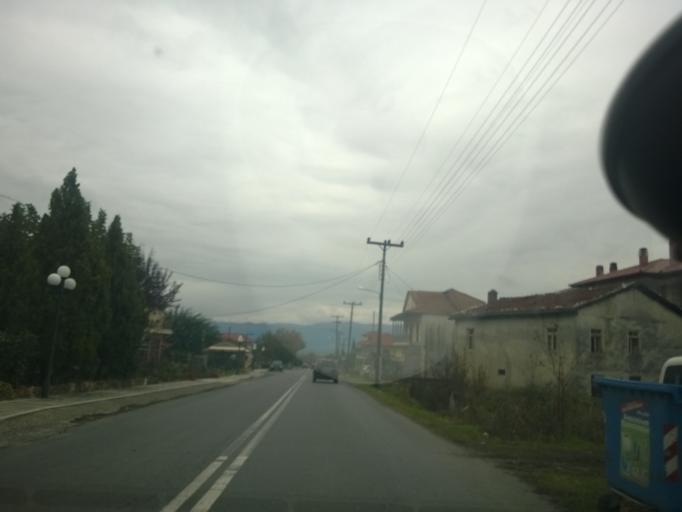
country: GR
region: Central Macedonia
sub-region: Nomos Pellis
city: Loutraki
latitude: 40.9703
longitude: 21.9512
